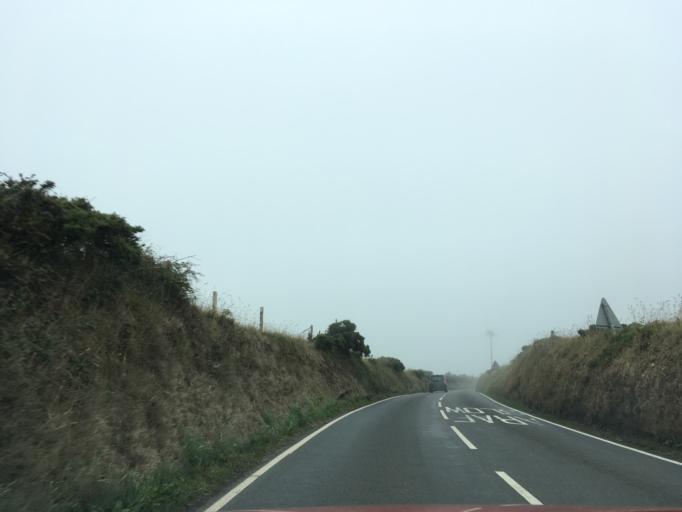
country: GB
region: Wales
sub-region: Pembrokeshire
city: Llanrhian
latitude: 51.8627
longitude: -5.1234
